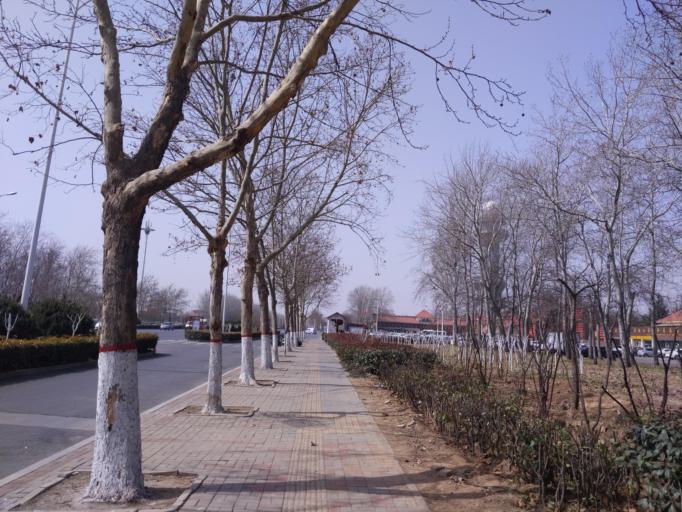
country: CN
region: Henan Sheng
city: Puyang
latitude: 35.7747
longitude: 114.9487
